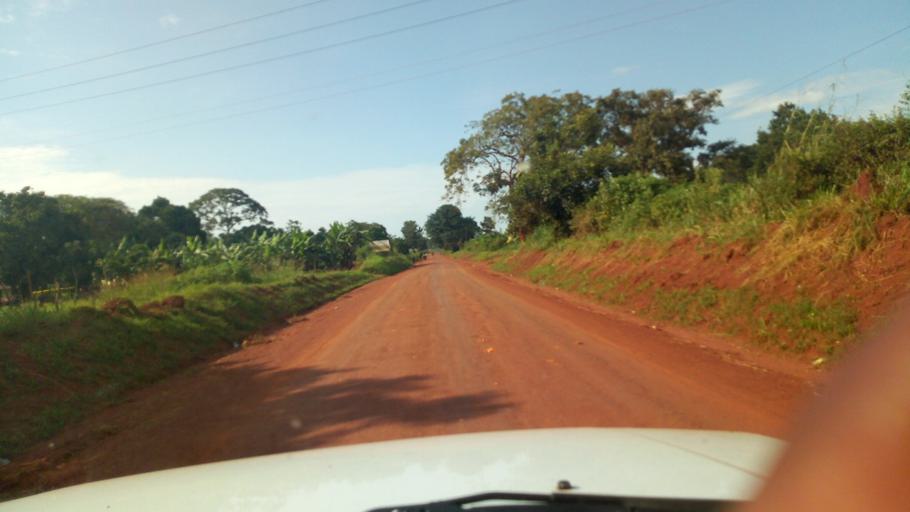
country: UG
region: Western Region
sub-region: Masindi District
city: Masindi
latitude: 1.6657
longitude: 31.7057
